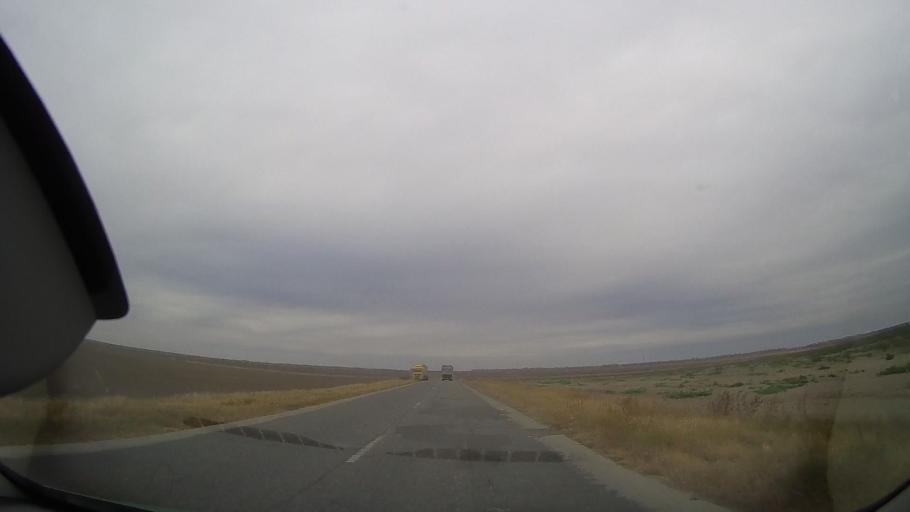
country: RO
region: Ialomita
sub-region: Comuna Milosesti
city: Milosesti
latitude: 44.7424
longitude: 27.2582
